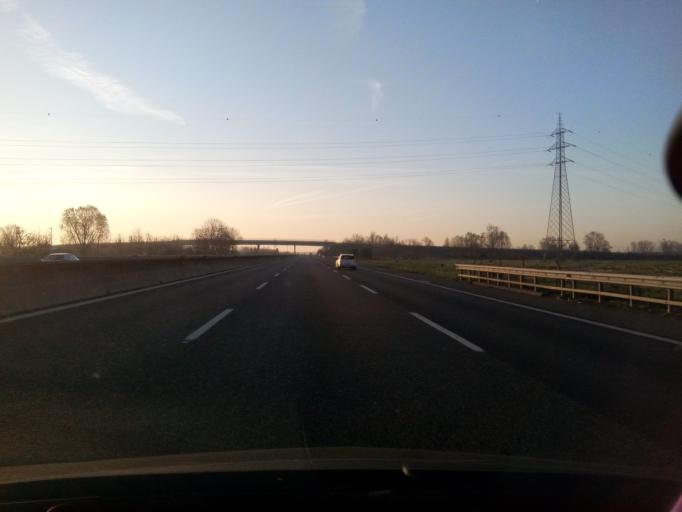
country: IT
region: Lombardy
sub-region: Provincia di Lodi
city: Salerano sul Lambro
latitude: 45.3092
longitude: 9.3947
